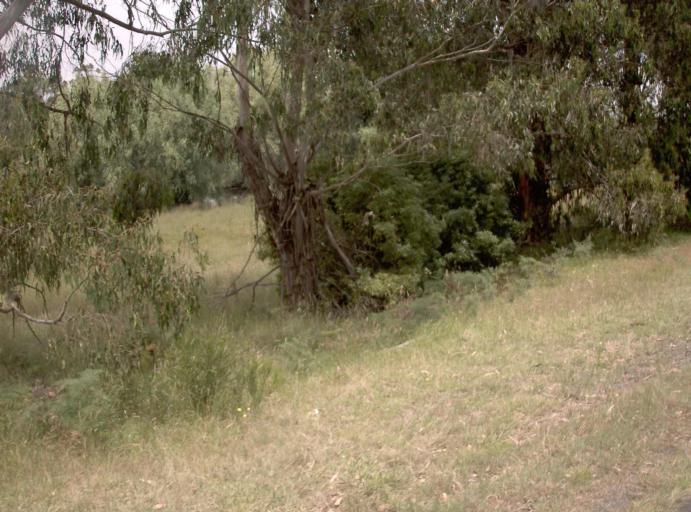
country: AU
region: Victoria
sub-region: Latrobe
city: Traralgon
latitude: -38.4631
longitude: 146.7206
